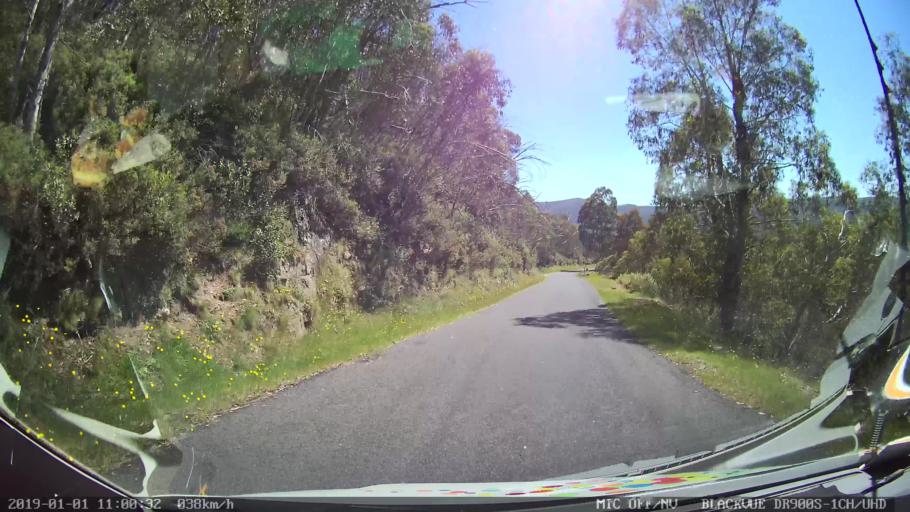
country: AU
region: New South Wales
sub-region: Snowy River
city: Jindabyne
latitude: -35.9802
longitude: 148.3977
